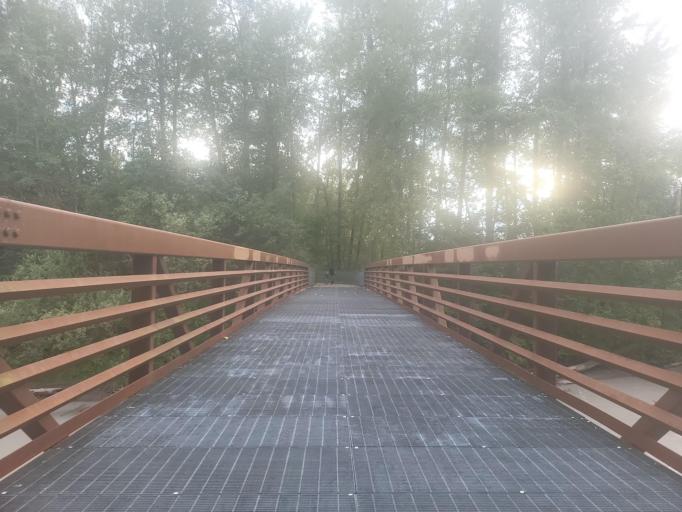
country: US
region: Washington
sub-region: King County
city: Pacific
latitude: 47.2446
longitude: -122.2350
